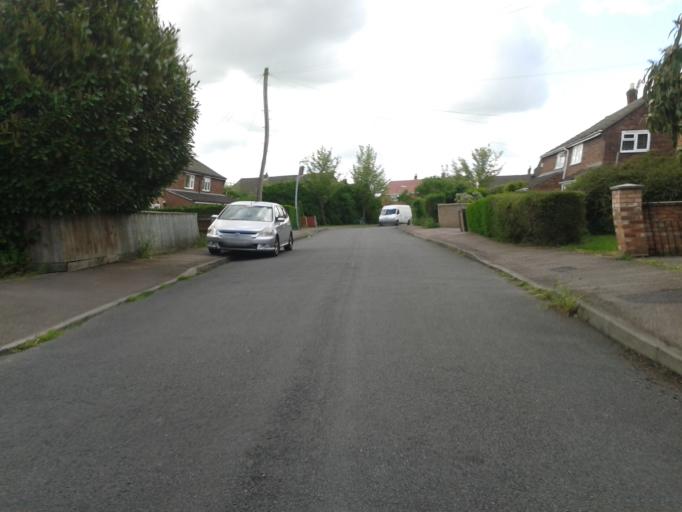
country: GB
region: England
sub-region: Cambridgeshire
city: Cambridge
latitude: 52.2217
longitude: 0.1560
